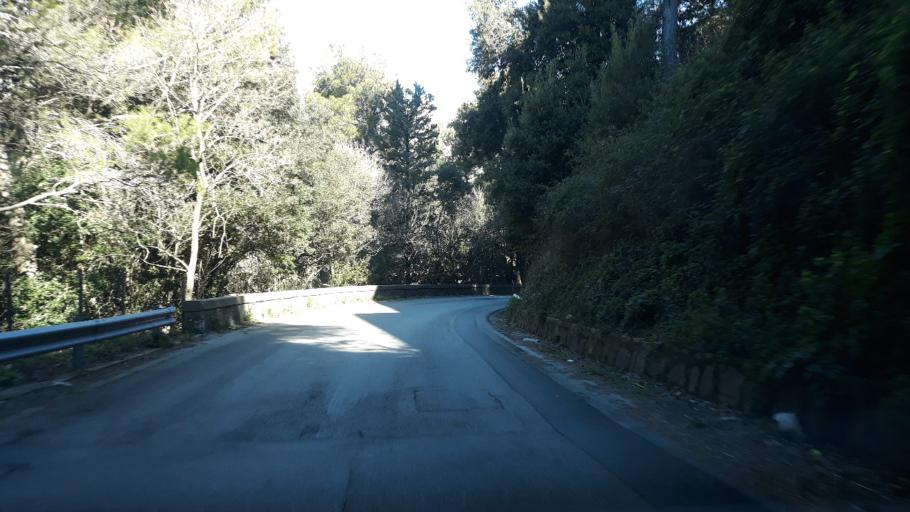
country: IT
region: Sicily
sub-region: Palermo
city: Piano dei Geli
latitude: 38.0915
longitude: 13.2536
